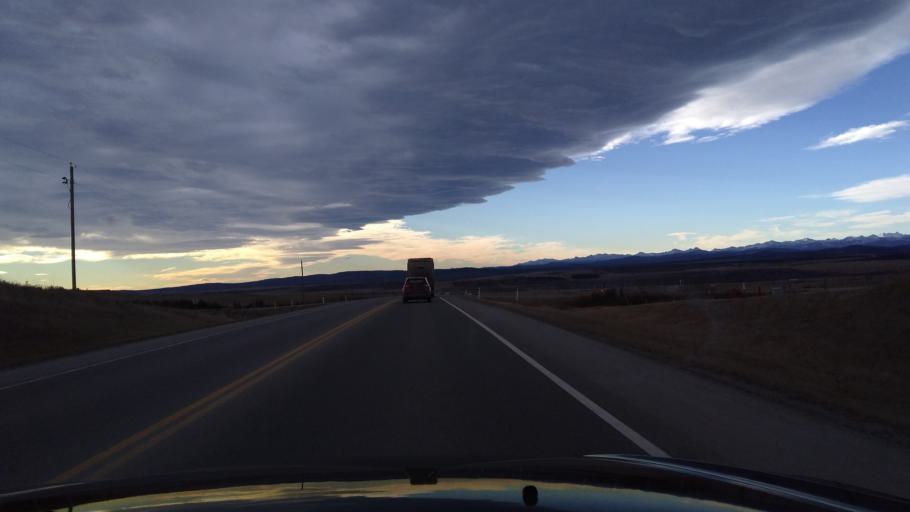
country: CA
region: Alberta
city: Cochrane
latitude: 51.1019
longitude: -114.4669
